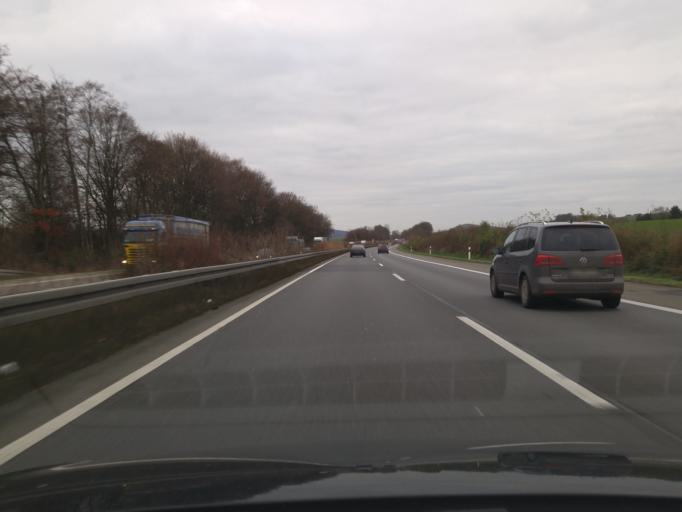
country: DE
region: Lower Saxony
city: Kalefeld
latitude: 51.8144
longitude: 10.1035
